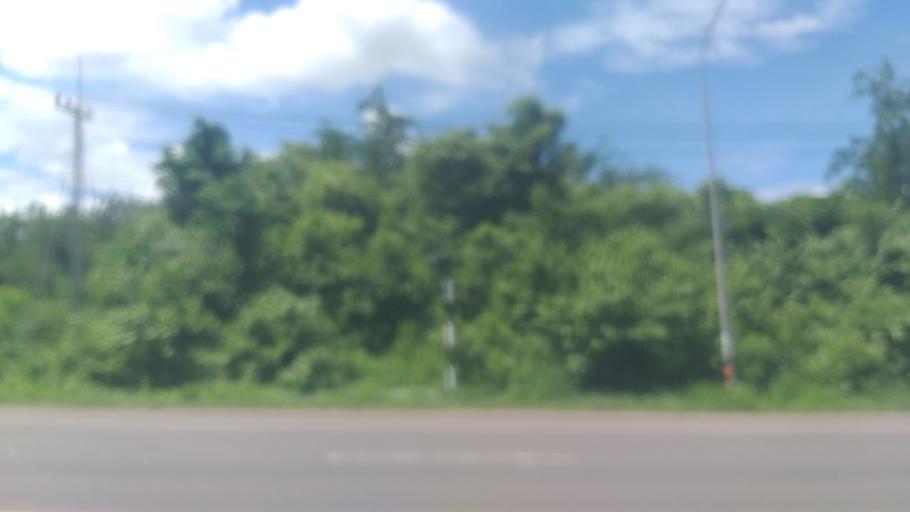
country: TH
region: Nakhon Ratchasima
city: Phra Thong Kham
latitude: 15.2986
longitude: 101.9823
